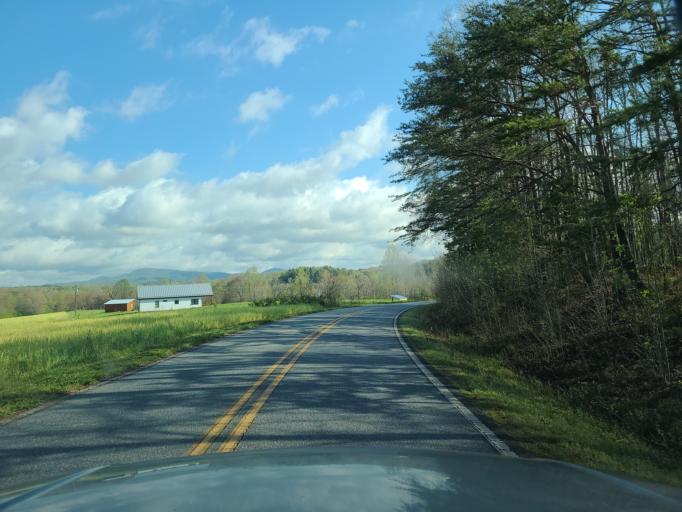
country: US
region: North Carolina
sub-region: Rutherford County
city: Forest City
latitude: 35.4039
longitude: -81.8233
